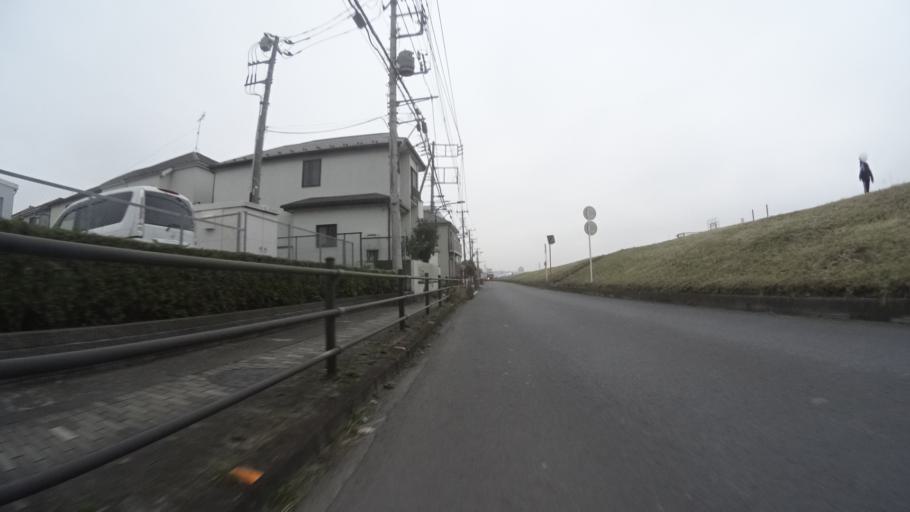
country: JP
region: Tokyo
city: Hino
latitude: 35.6733
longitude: 139.4291
